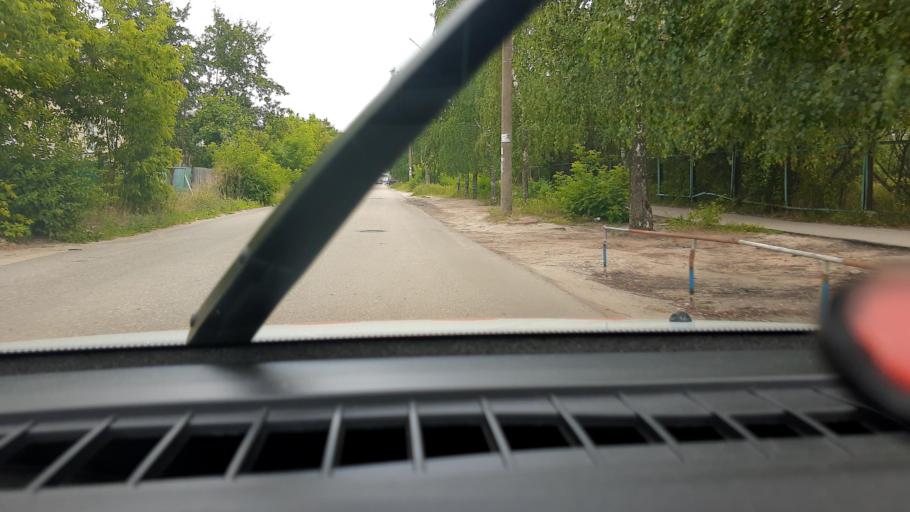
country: RU
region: Nizjnij Novgorod
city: Dzerzhinsk
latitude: 56.2403
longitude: 43.4324
